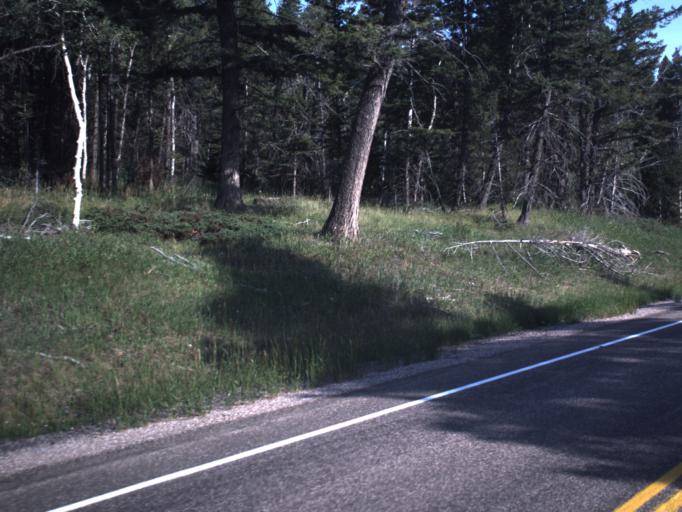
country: US
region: Utah
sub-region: Uintah County
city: Maeser
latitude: 40.7329
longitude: -109.4705
